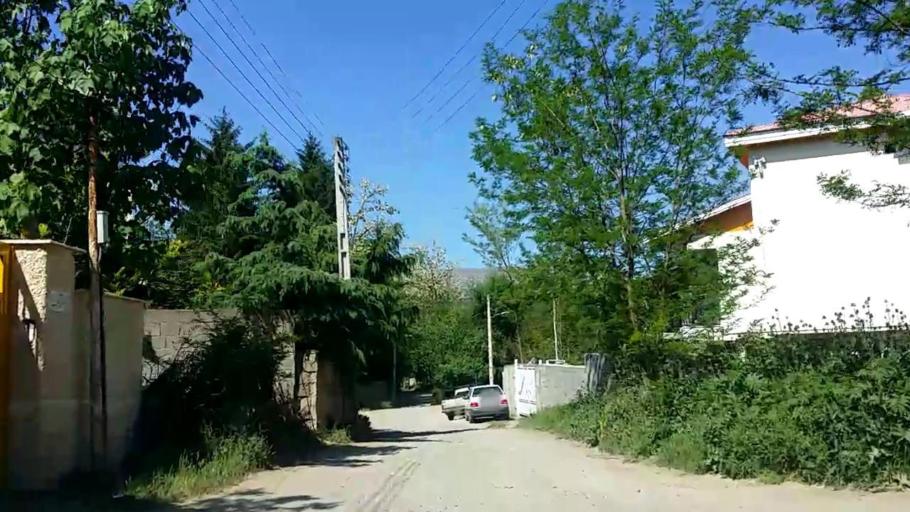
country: IR
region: Mazandaran
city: `Abbasabad
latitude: 36.5091
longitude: 51.1891
